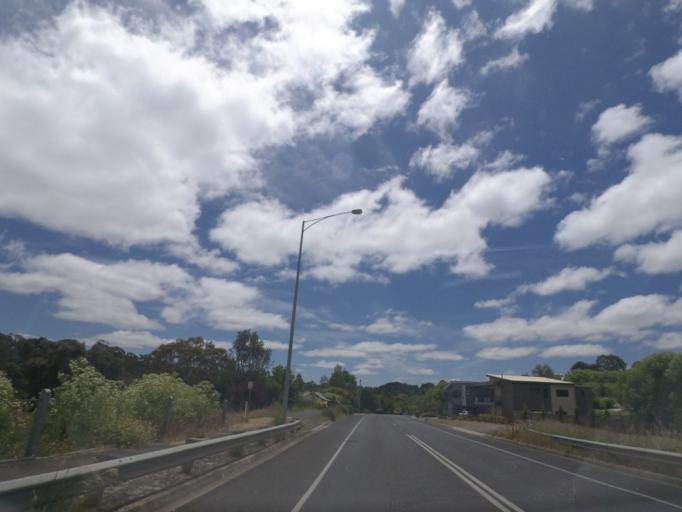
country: AU
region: Victoria
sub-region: Mount Alexander
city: Castlemaine
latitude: -37.3538
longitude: 144.1405
